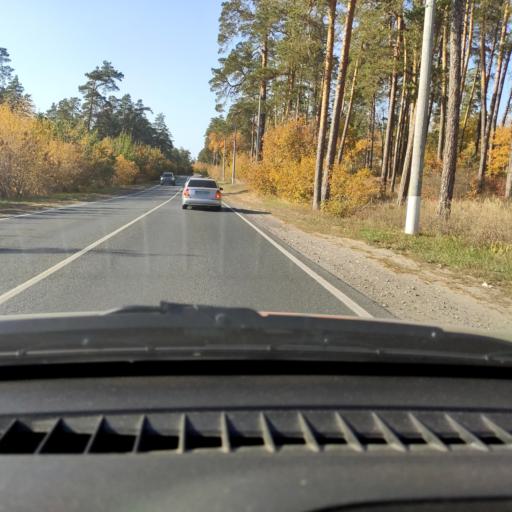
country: RU
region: Samara
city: Tol'yatti
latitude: 53.4733
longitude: 49.3849
